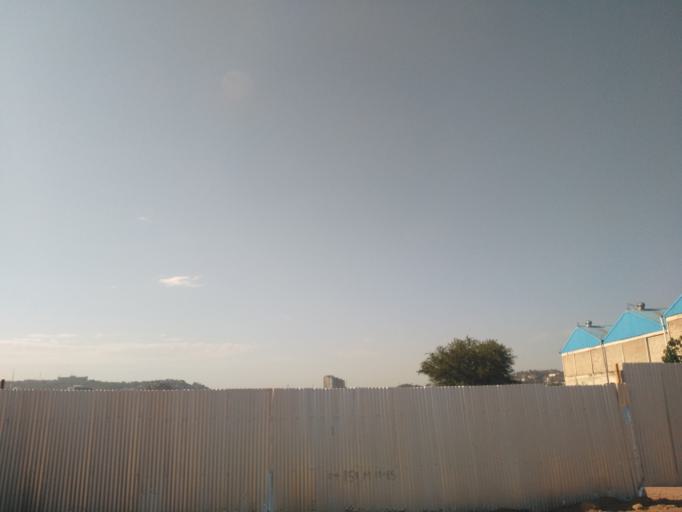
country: TZ
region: Mwanza
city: Mwanza
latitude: -2.5065
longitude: 32.8937
